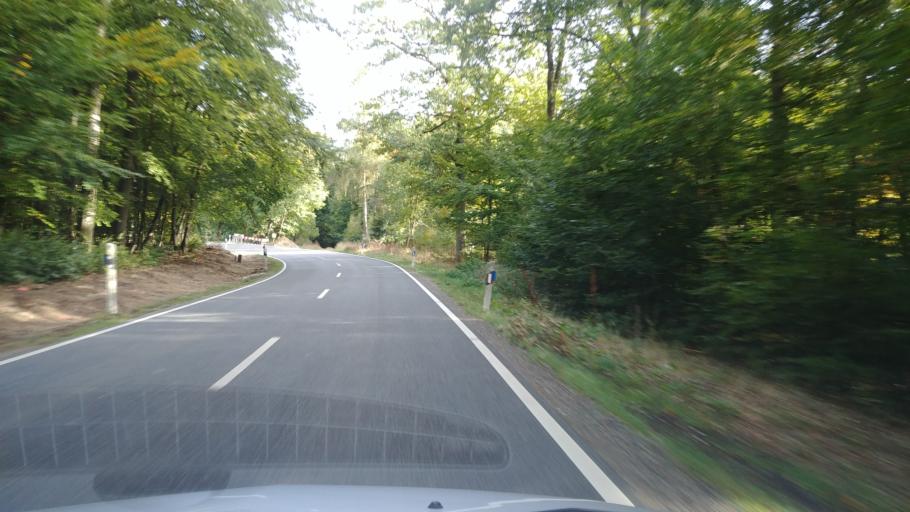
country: DE
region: Rheinland-Pfalz
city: Reckenroth
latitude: 50.2023
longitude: 8.0078
